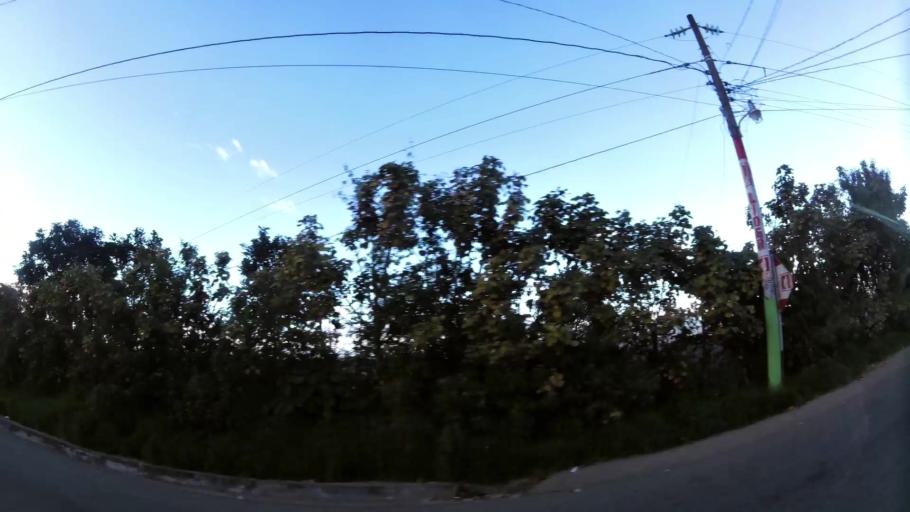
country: GT
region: Quiche
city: Chichicastenango
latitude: 14.9358
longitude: -91.1091
